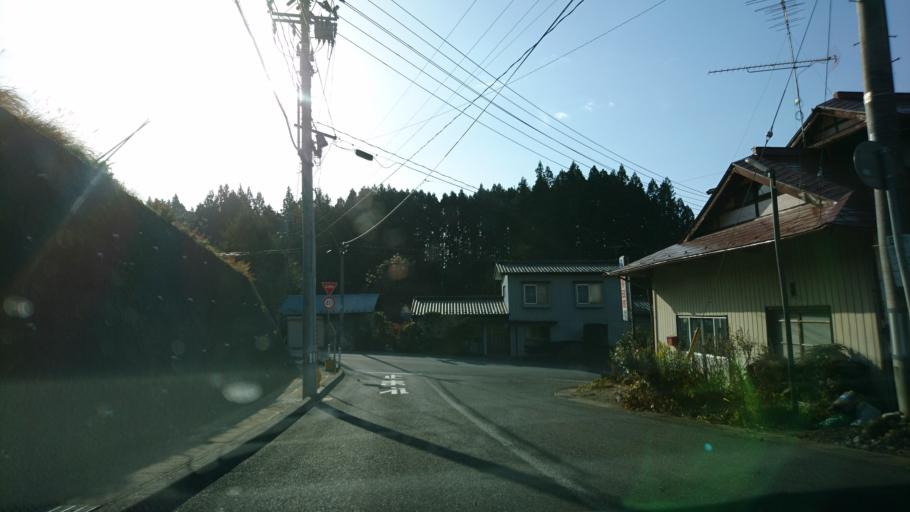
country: JP
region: Iwate
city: Ichinoseki
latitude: 38.8598
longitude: 141.3420
